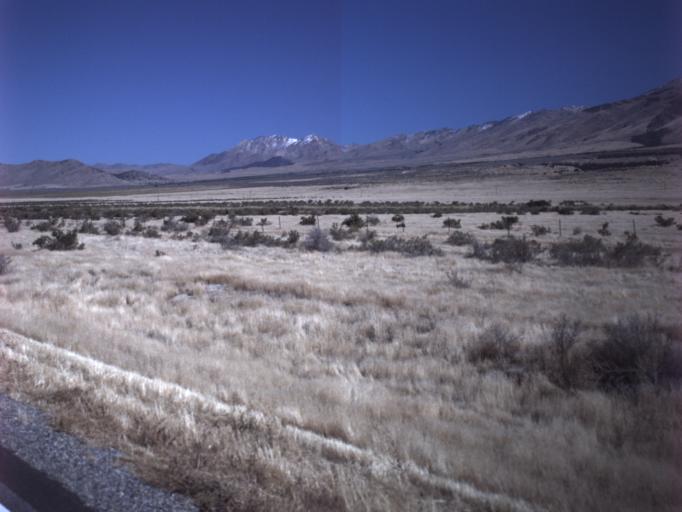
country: US
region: Utah
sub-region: Tooele County
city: Grantsville
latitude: 40.4685
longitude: -112.7466
